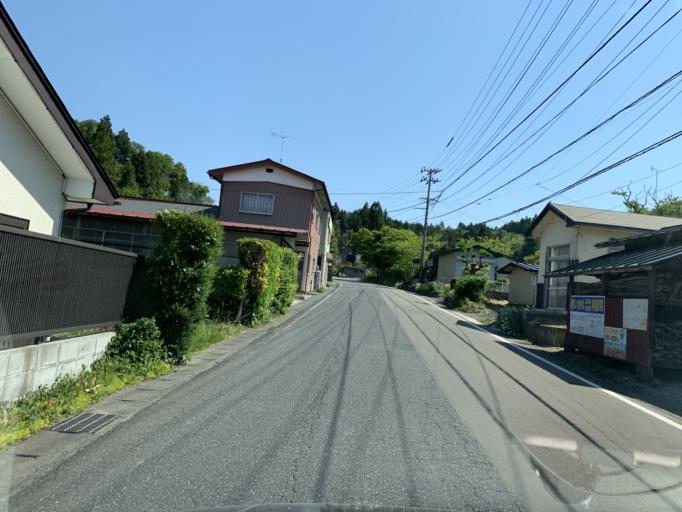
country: JP
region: Iwate
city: Mizusawa
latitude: 39.0421
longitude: 141.0647
